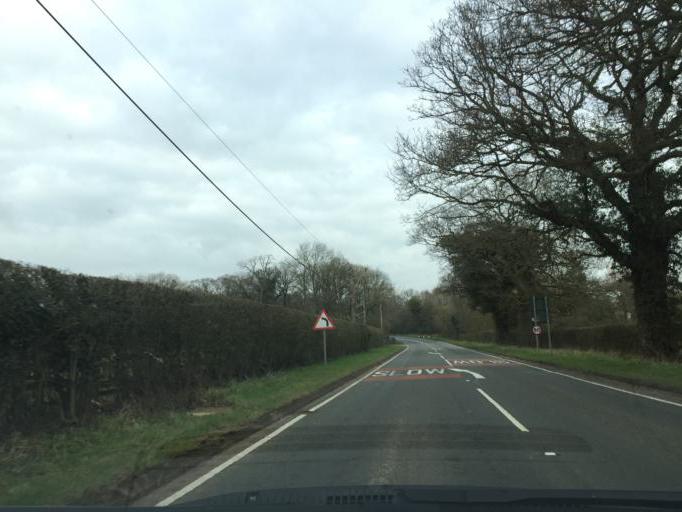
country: GB
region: England
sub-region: Warwickshire
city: Henley in Arden
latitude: 52.2959
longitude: -1.8278
